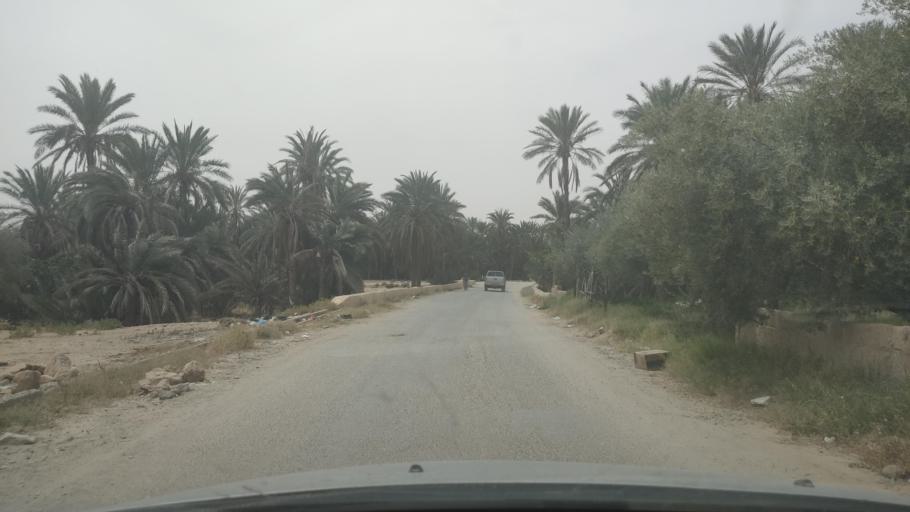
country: TN
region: Gafsa
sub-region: Gafsa Municipality
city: Gafsa
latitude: 34.3302
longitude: 8.9529
